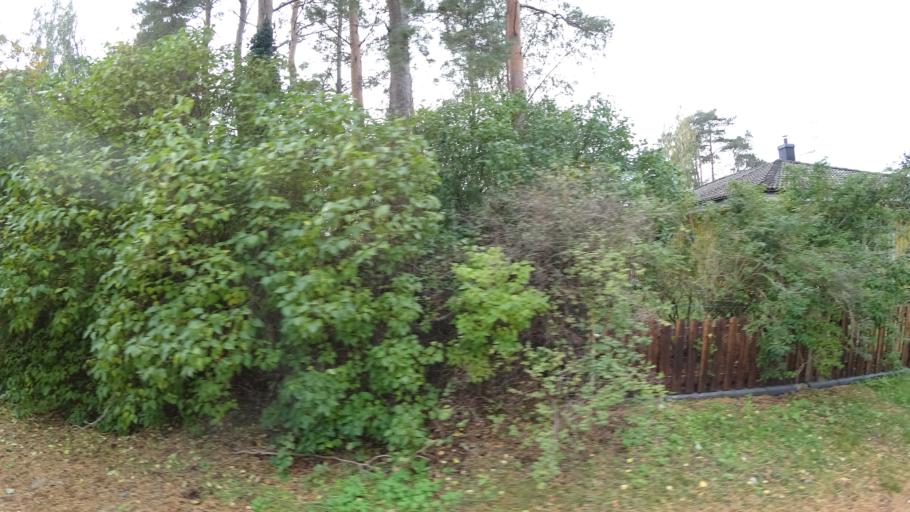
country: SE
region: Skane
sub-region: Kavlinge Kommun
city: Hofterup
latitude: 55.8018
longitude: 12.9888
